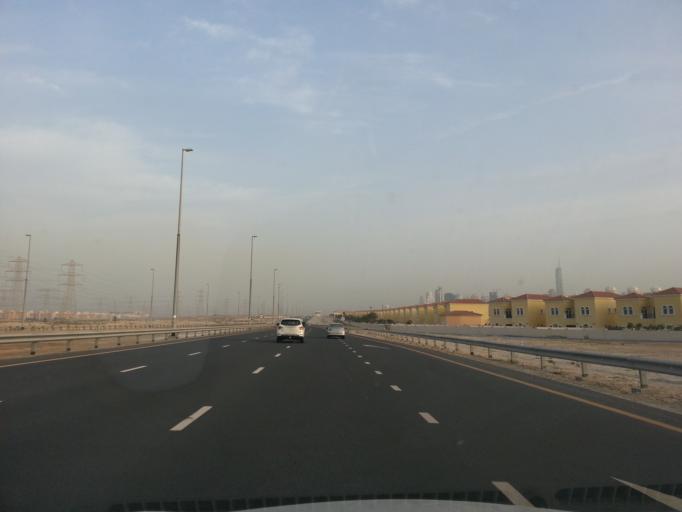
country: AE
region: Dubai
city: Dubai
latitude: 25.0417
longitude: 55.1553
